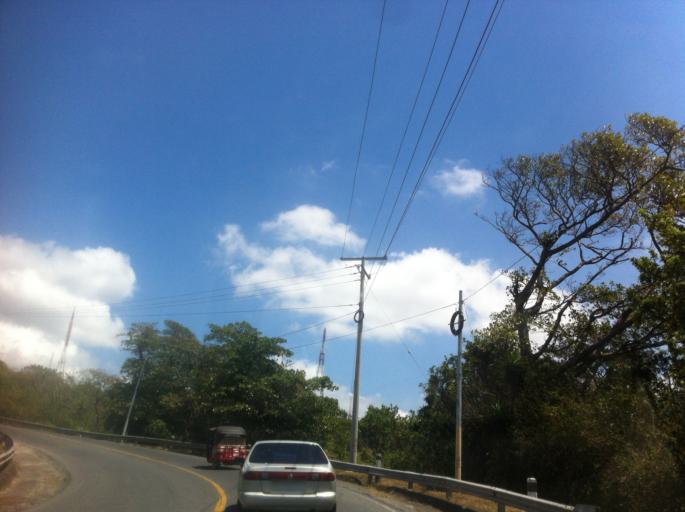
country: NI
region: Managua
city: El Crucero
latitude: 11.9970
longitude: -86.3139
